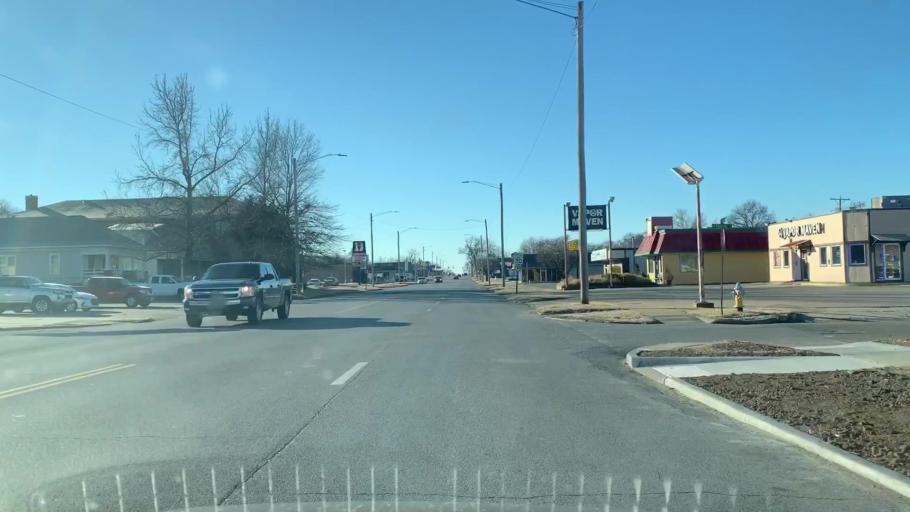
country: US
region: Kansas
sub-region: Crawford County
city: Pittsburg
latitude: 37.4055
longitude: -94.7050
